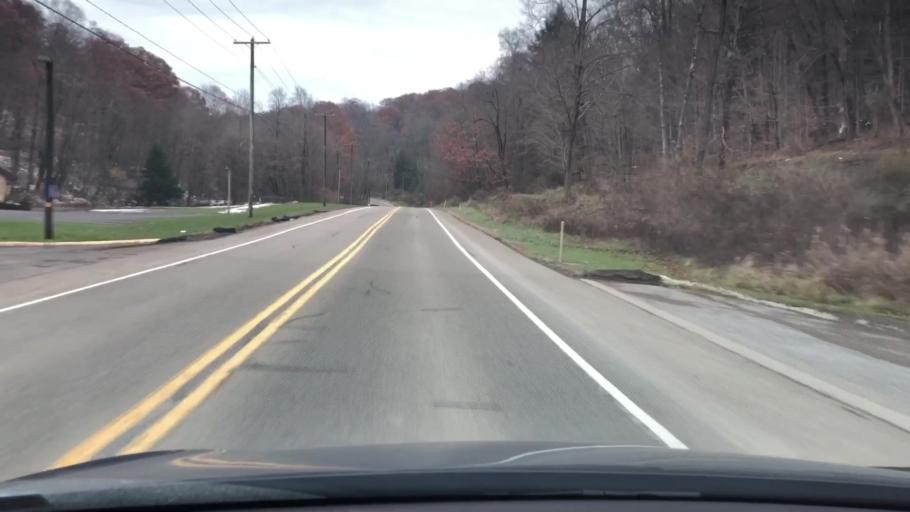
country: US
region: Pennsylvania
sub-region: Clarion County
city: Clarion
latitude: 40.9895
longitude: -79.3442
